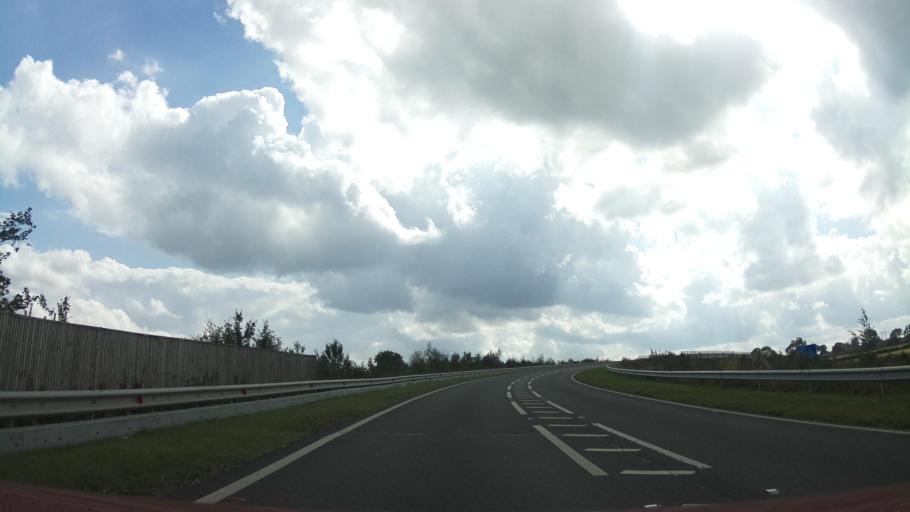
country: GB
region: England
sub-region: Darlington
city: High Coniscliffe
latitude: 54.4547
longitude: -1.6664
